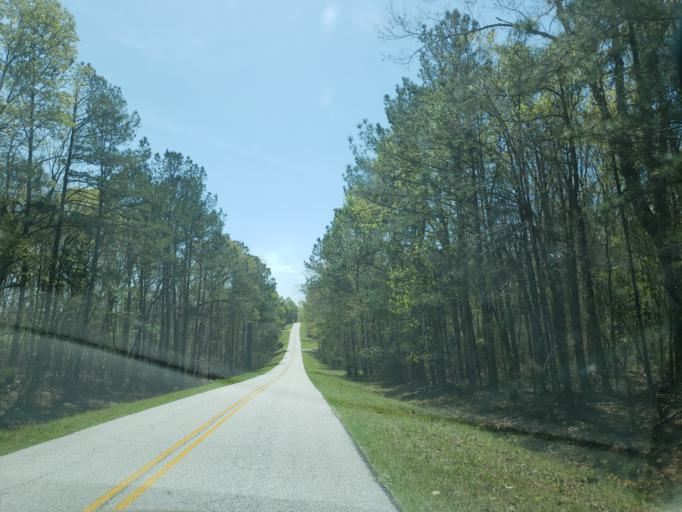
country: US
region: Alabama
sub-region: Elmore County
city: Tallassee
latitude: 32.6821
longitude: -85.8647
